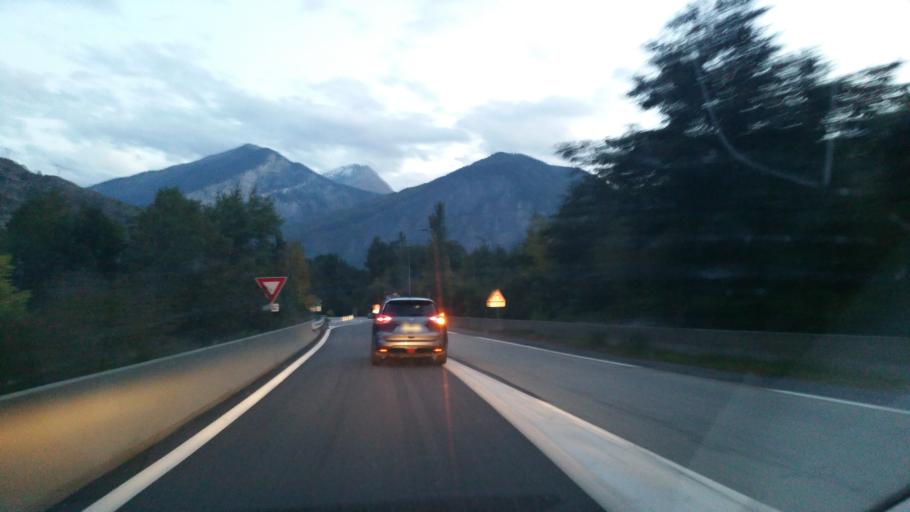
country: FR
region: Rhone-Alpes
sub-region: Departement de la Savoie
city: Saint-Jean-de-Maurienne
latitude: 45.2951
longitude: 6.3546
